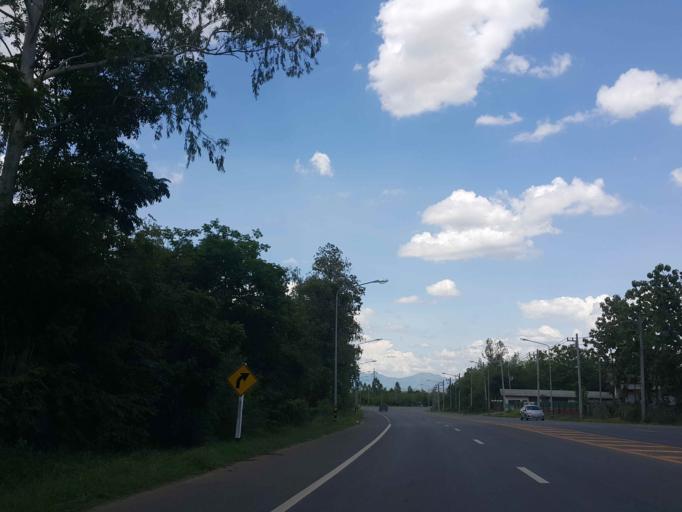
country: TH
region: Phrae
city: Nong Muang Khai
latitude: 18.2038
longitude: 100.2078
